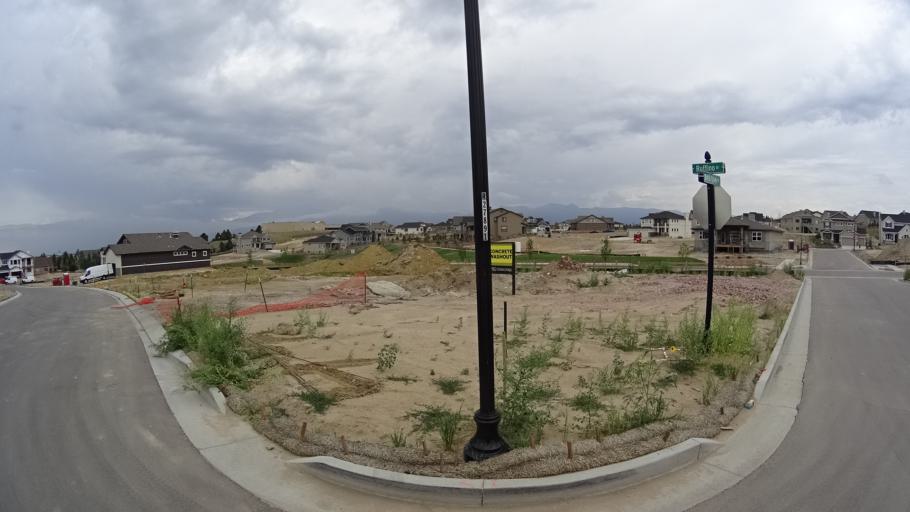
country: US
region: Colorado
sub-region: El Paso County
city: Gleneagle
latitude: 39.0073
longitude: -104.7897
